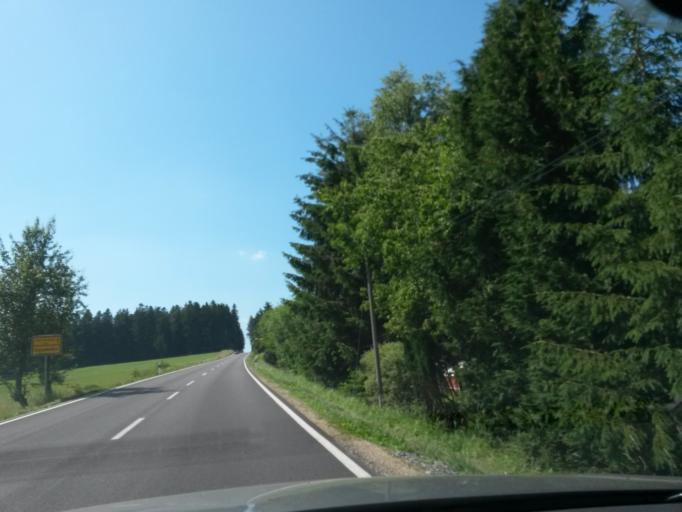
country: DE
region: Baden-Wuerttemberg
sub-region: Karlsruhe Region
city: Oberreichenbach
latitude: 48.7356
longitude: 8.6576
